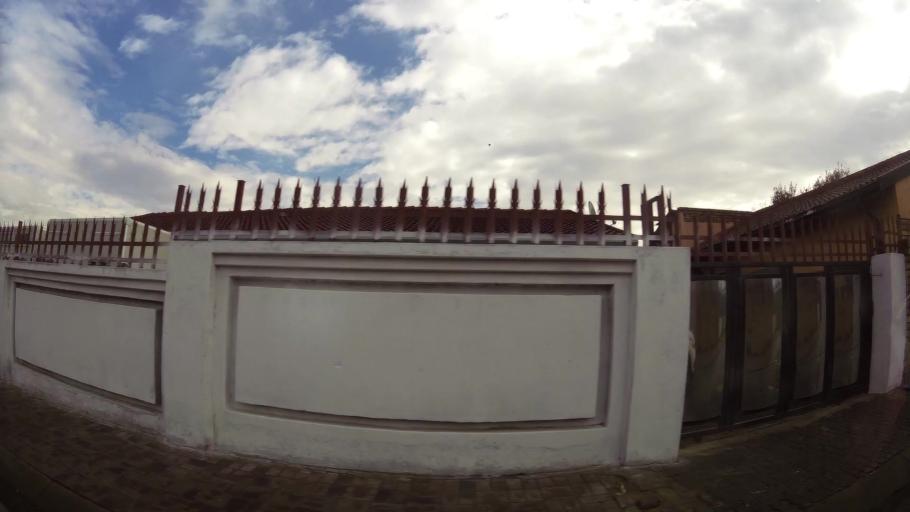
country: ZA
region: Gauteng
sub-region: Ekurhuleni Metropolitan Municipality
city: Germiston
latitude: -26.3280
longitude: 28.1847
